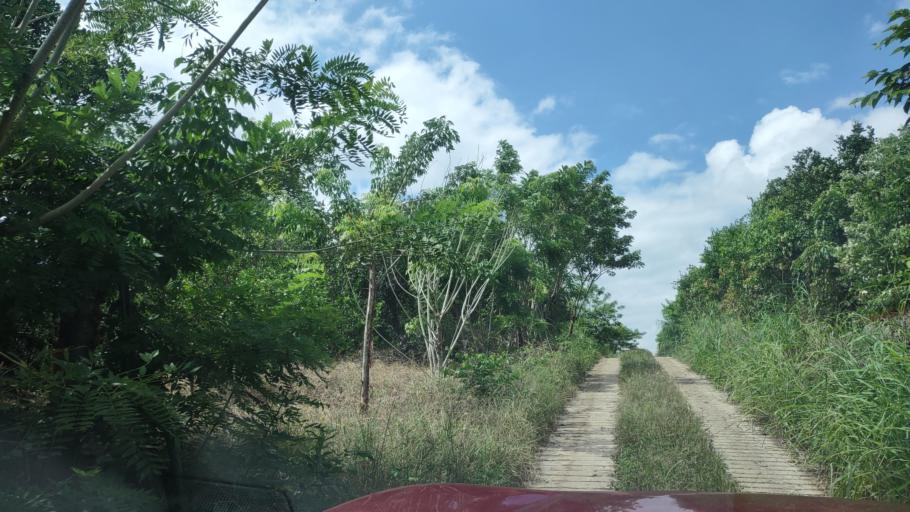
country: MX
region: Puebla
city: San Jose Acateno
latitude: 20.2228
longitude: -97.1523
